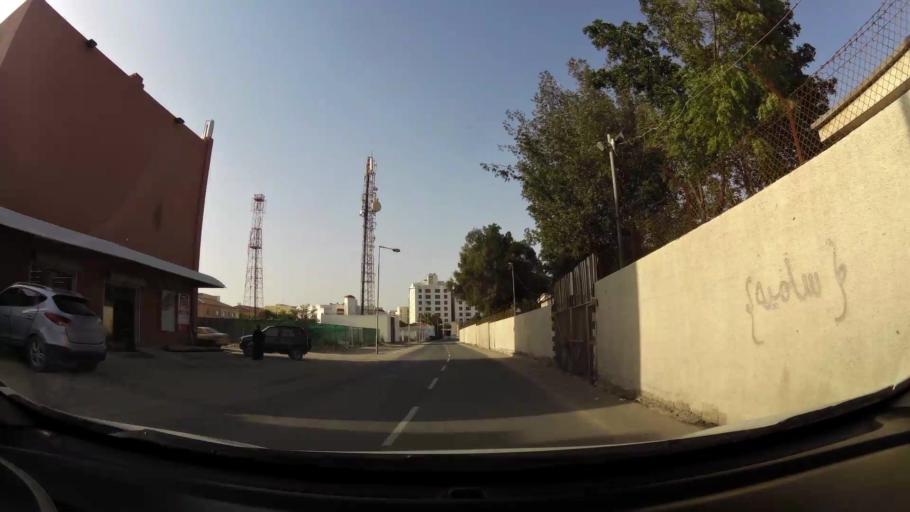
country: BH
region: Manama
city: Jidd Hafs
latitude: 26.2187
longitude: 50.5041
